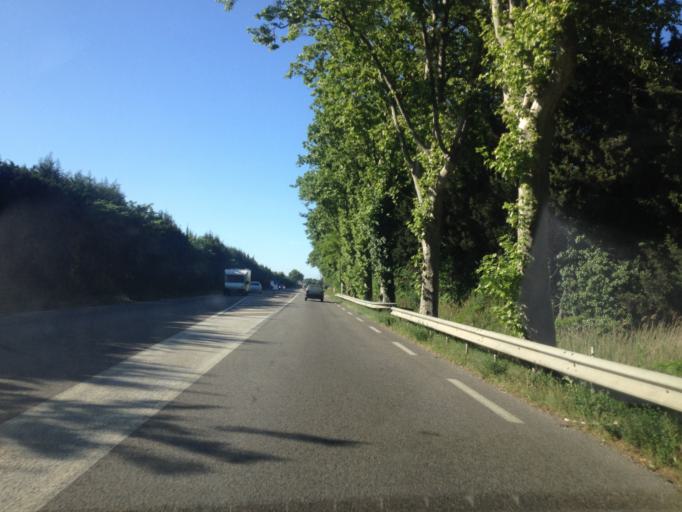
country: FR
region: Provence-Alpes-Cote d'Azur
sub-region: Departement du Vaucluse
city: Courthezon
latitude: 44.0762
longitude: 4.8820
